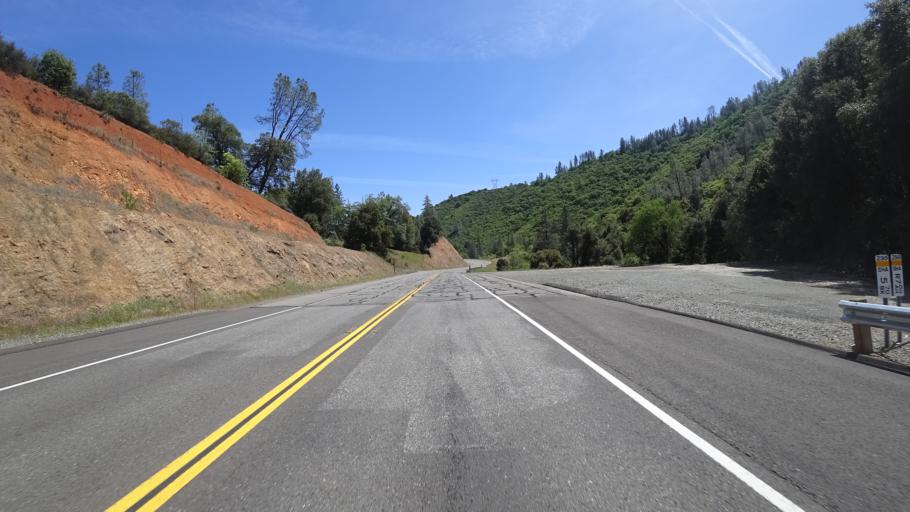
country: US
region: California
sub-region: Trinity County
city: Lewiston
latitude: 40.6729
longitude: -122.6623
